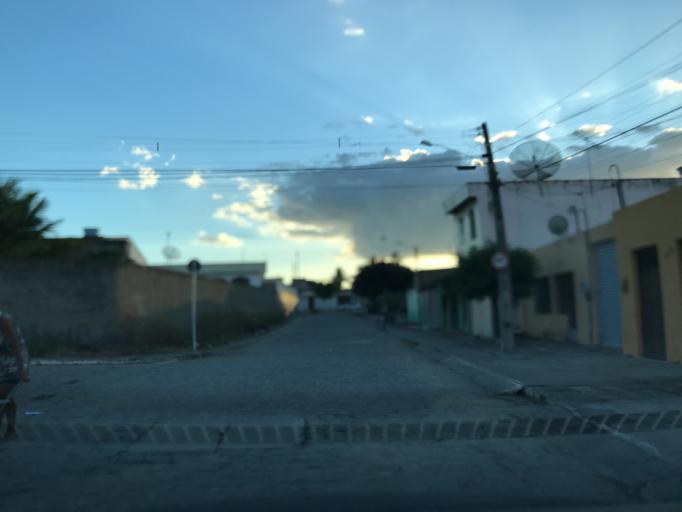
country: BR
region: Pernambuco
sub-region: Bezerros
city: Bezerros
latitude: -8.2418
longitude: -35.7590
